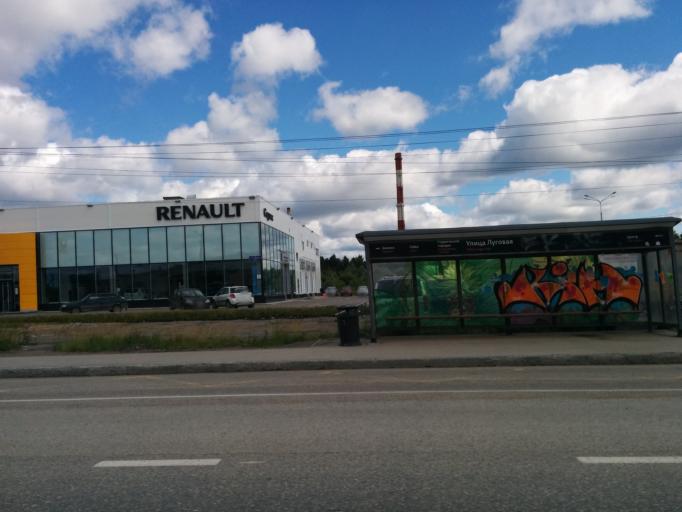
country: RU
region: Perm
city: Perm
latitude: 58.0361
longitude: 56.1977
